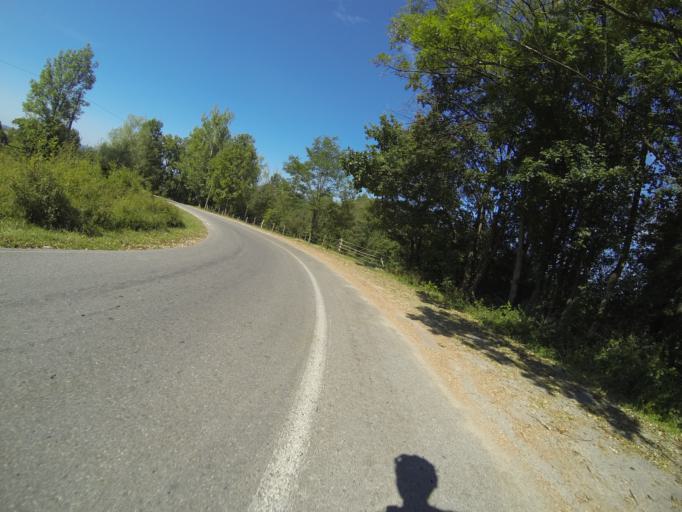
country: RO
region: Gorj
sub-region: Comuna Polovragi
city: Polovragi
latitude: 45.1700
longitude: 23.8471
